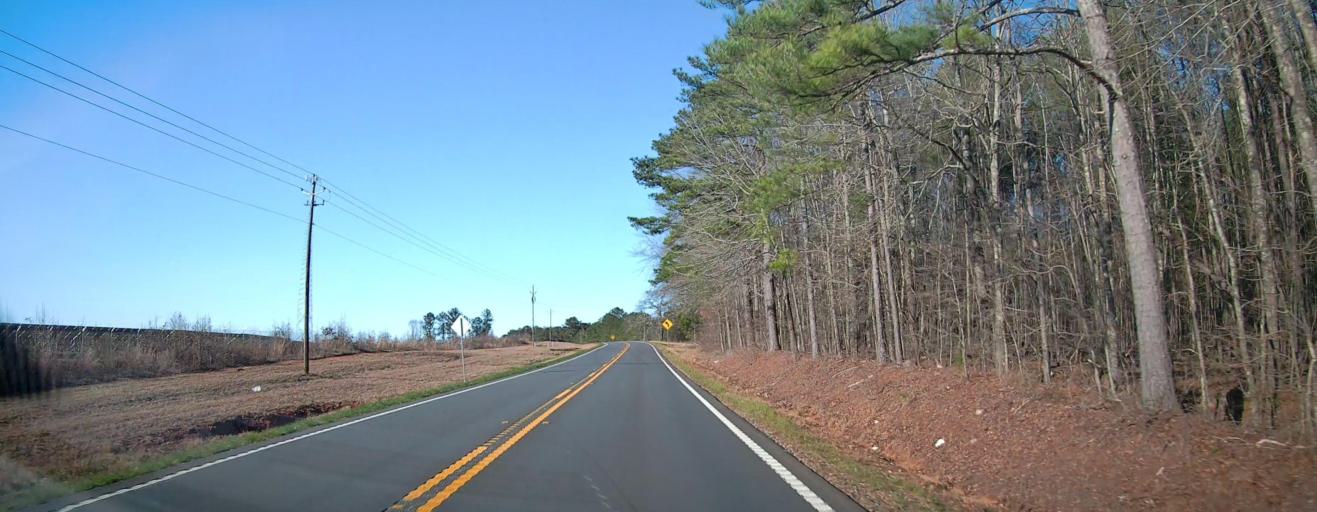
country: US
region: Georgia
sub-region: Talbot County
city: Sardis
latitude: 32.7950
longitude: -84.6929
